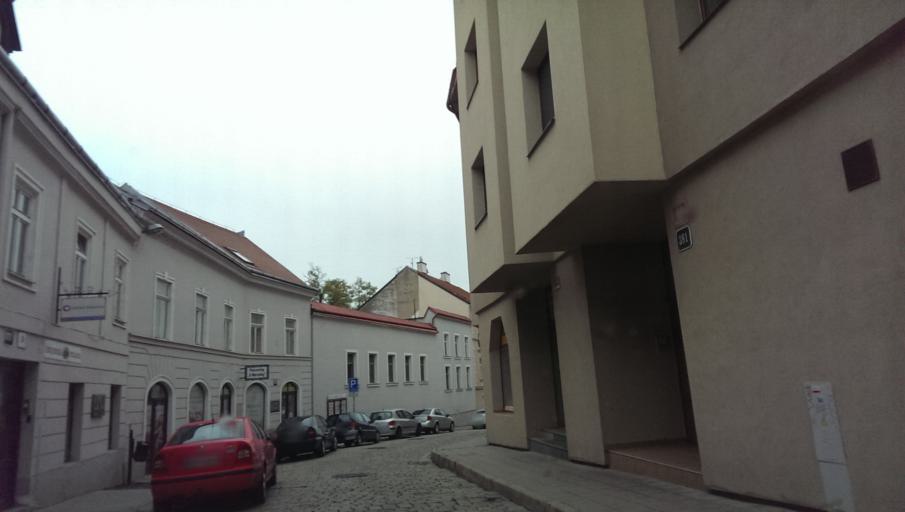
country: CZ
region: South Moravian
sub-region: Okres Znojmo
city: Znojmo
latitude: 48.8535
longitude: 16.0516
